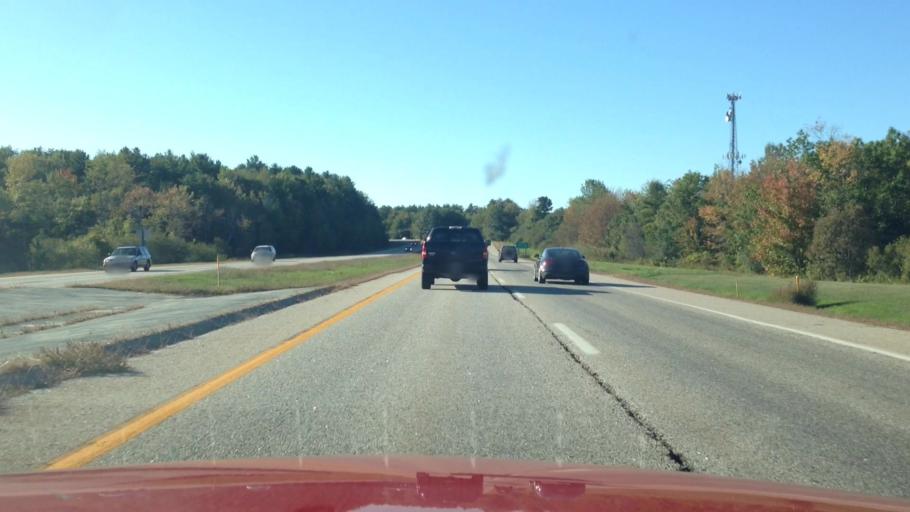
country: US
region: Maine
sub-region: Cumberland County
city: Westbrook
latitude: 43.6712
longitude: -70.3385
